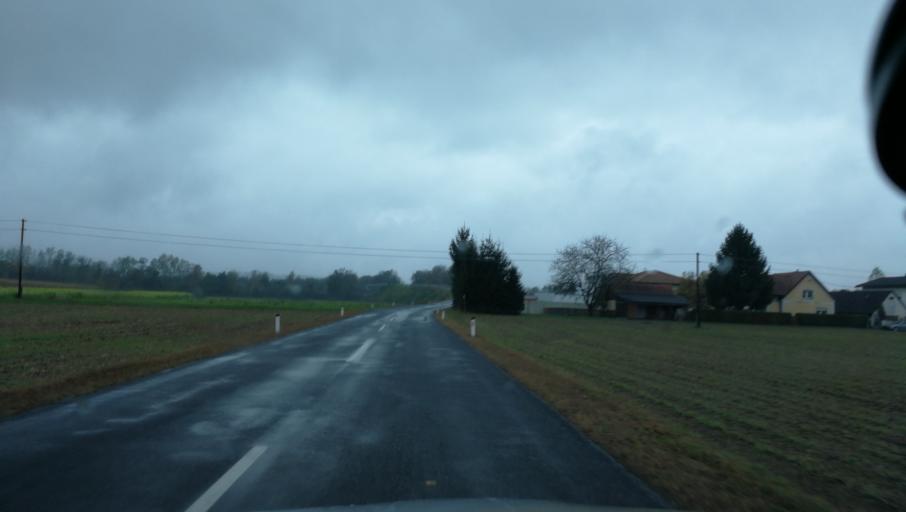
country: AT
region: Styria
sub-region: Politischer Bezirk Leibnitz
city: Sankt Veit am Vogau
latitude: 46.7437
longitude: 15.6210
